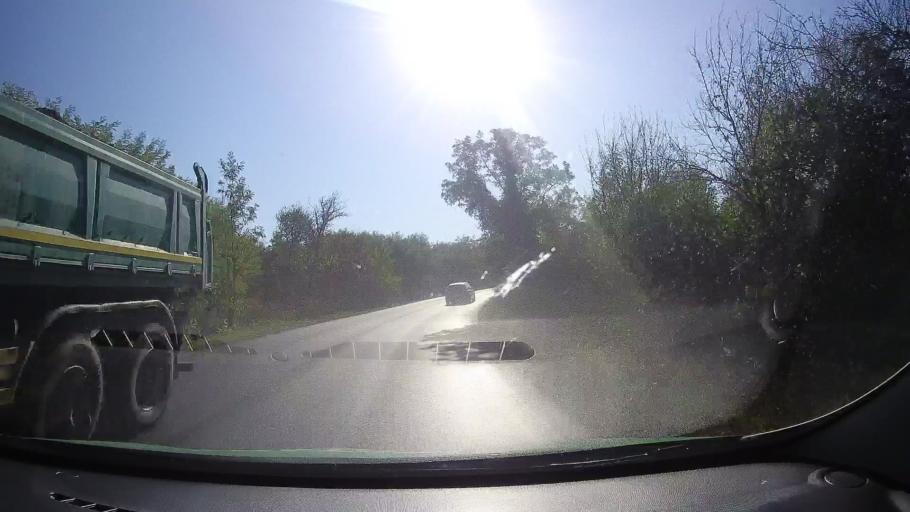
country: RO
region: Timis
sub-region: Comuna Curtea
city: Curtea
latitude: 45.8487
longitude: 22.3210
